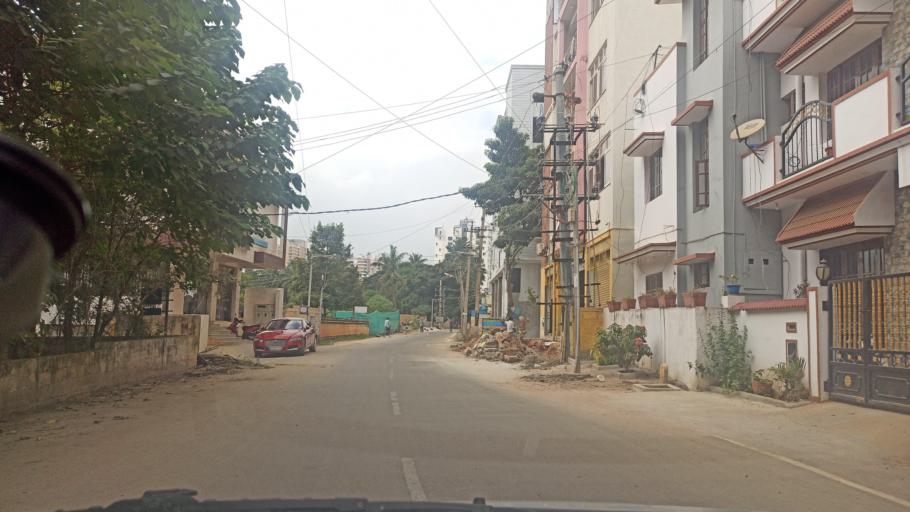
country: IN
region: Karnataka
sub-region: Bangalore Urban
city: Yelahanka
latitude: 13.0487
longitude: 77.6097
